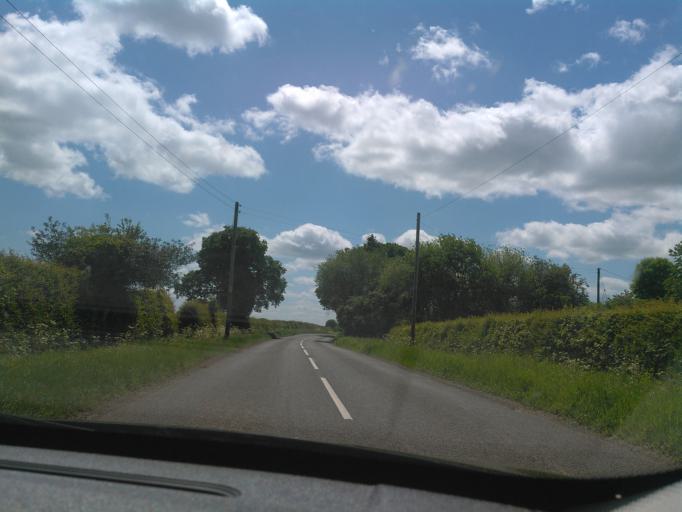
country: GB
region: England
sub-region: Shropshire
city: Wem
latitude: 52.8783
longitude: -2.7156
